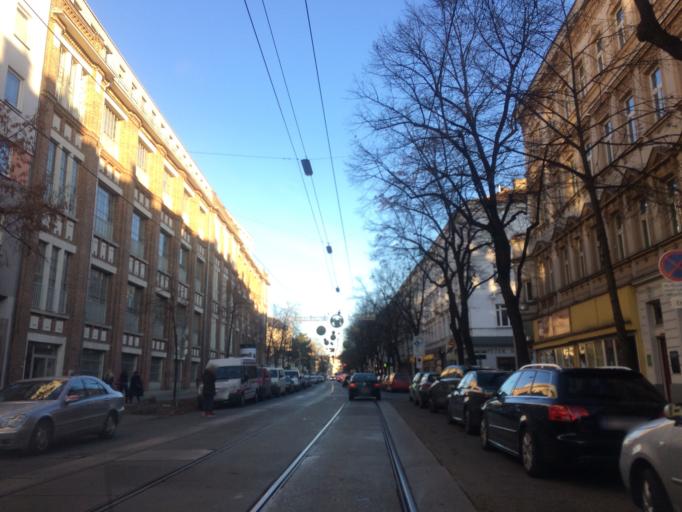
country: AT
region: Vienna
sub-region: Wien Stadt
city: Vienna
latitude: 48.1977
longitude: 16.2993
